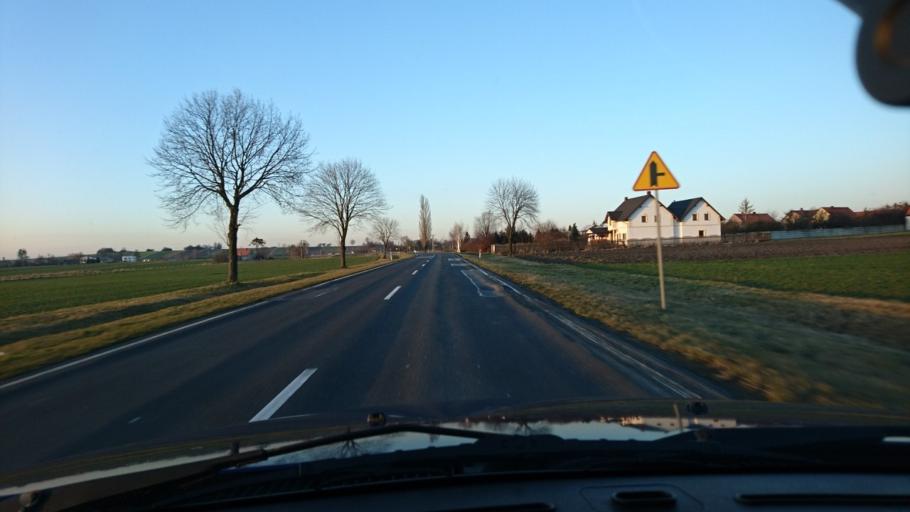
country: PL
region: Silesian Voivodeship
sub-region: Powiat gliwicki
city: Wielowies
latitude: 50.4684
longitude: 18.6106
